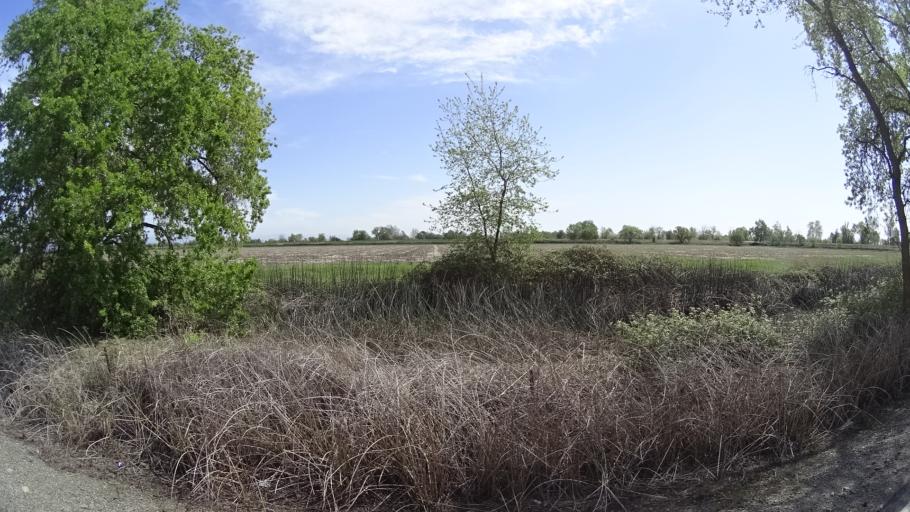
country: US
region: California
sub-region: Butte County
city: Durham
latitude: 39.5390
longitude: -121.8565
